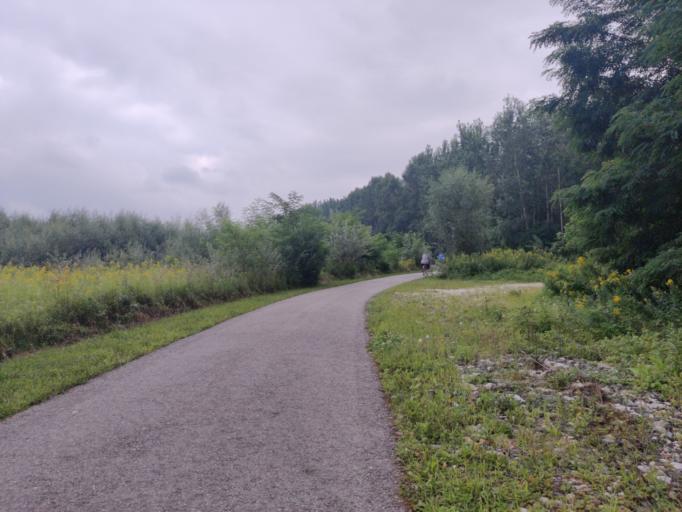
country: AT
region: Lower Austria
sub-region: Politischer Bezirk Tulln
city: Kirchberg am Wagram
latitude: 48.3621
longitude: 15.8749
